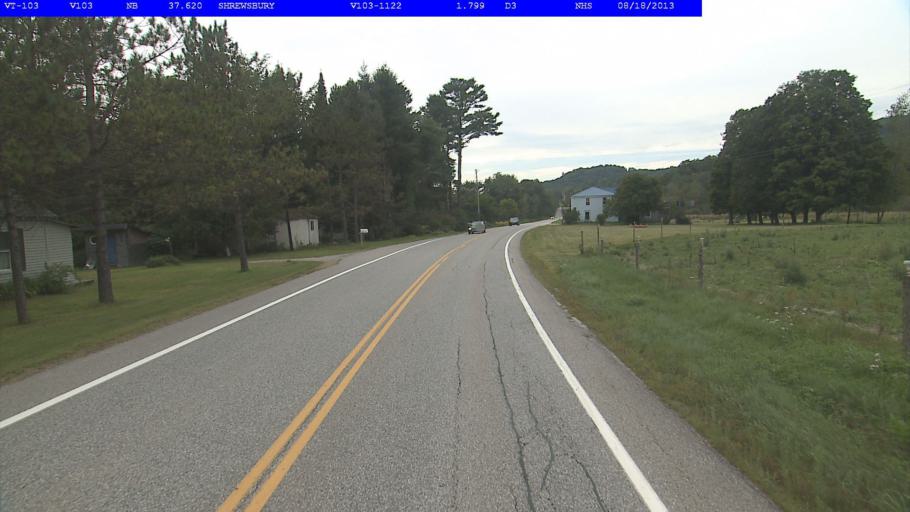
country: US
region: Vermont
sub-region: Rutland County
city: Rutland
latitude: 43.4996
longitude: -72.8970
